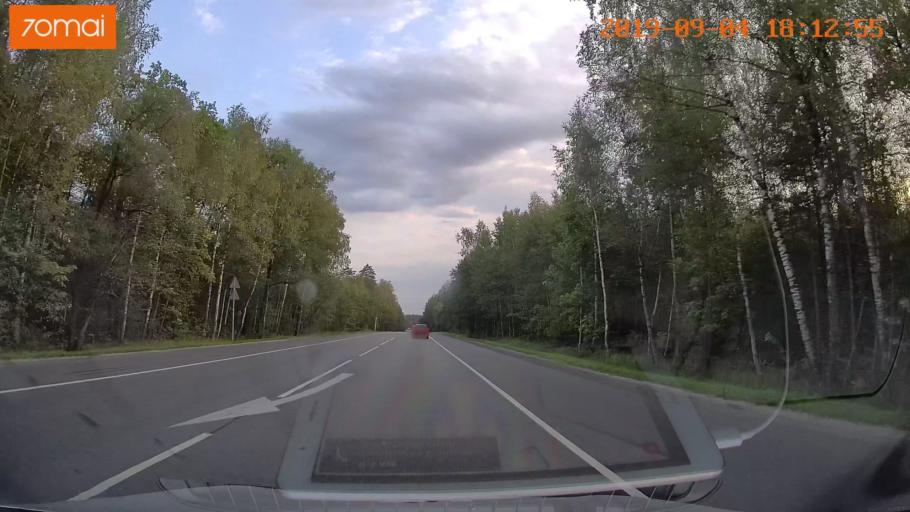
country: RU
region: Moskovskaya
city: Lopatinskiy
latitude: 55.3663
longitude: 38.7365
